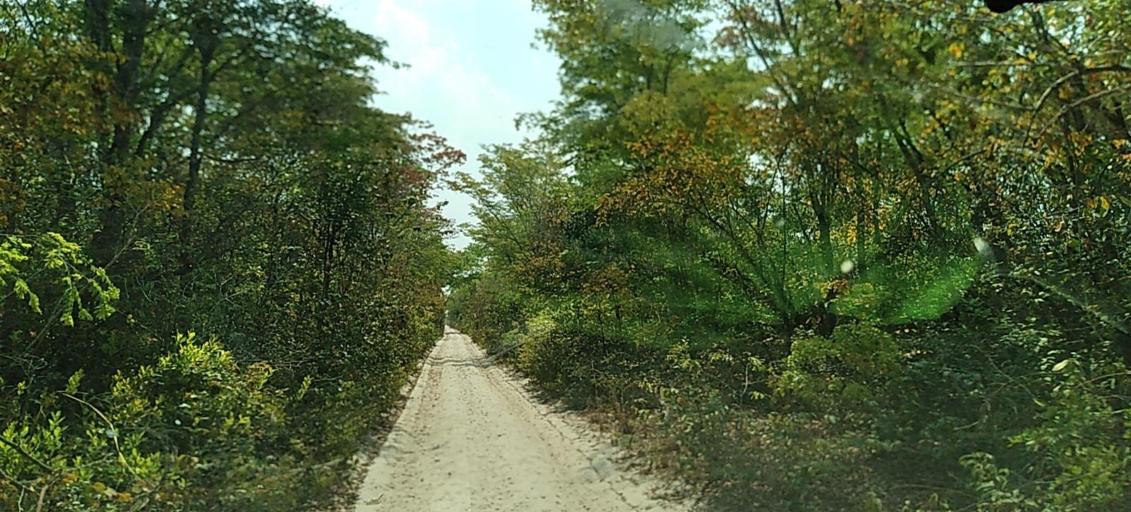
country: ZM
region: North-Western
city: Kabompo
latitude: -13.3945
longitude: 23.7948
